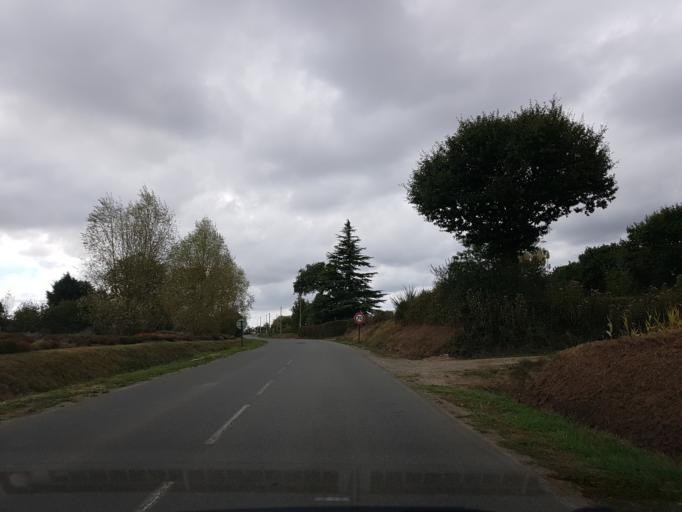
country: FR
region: Brittany
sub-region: Departement des Cotes-d'Armor
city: Quessoy
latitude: 48.4437
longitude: -2.6490
